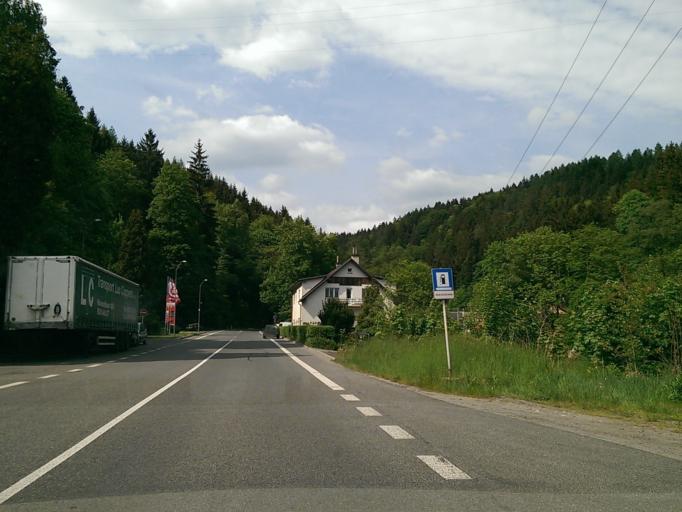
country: CZ
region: Liberecky
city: Zelezny Brod
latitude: 50.6470
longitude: 15.2557
